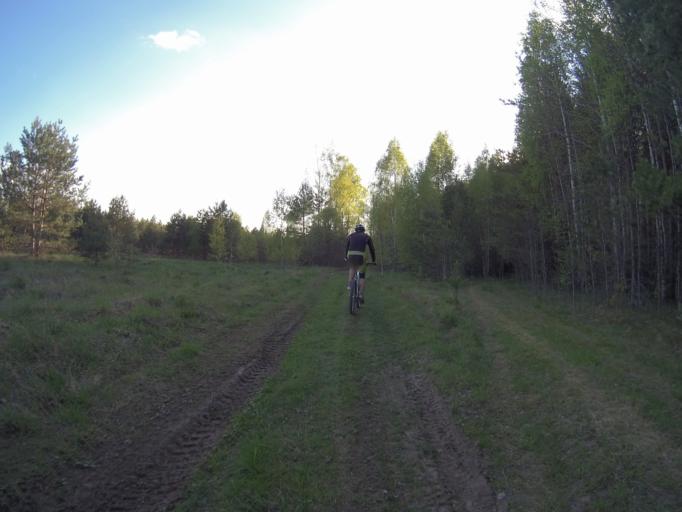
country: RU
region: Vladimir
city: Orgtrud
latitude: 56.0736
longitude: 40.7291
